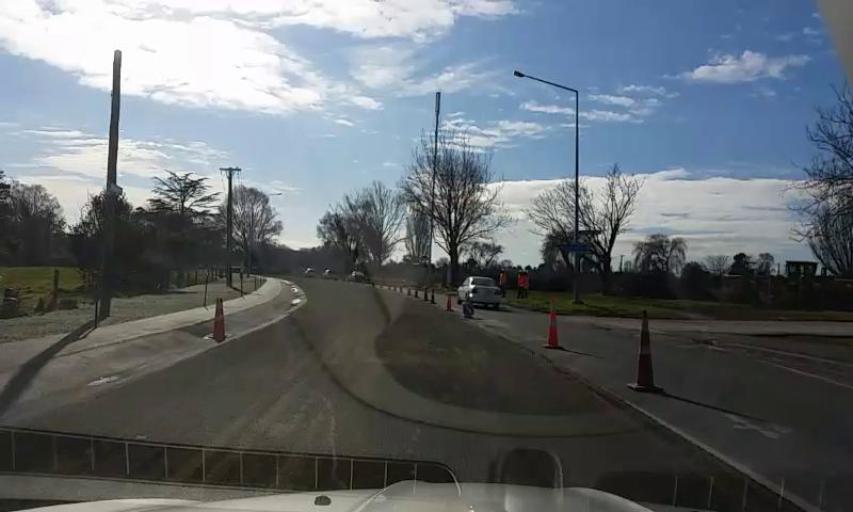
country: NZ
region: Canterbury
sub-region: Christchurch City
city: Christchurch
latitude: -43.5048
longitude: 172.6813
